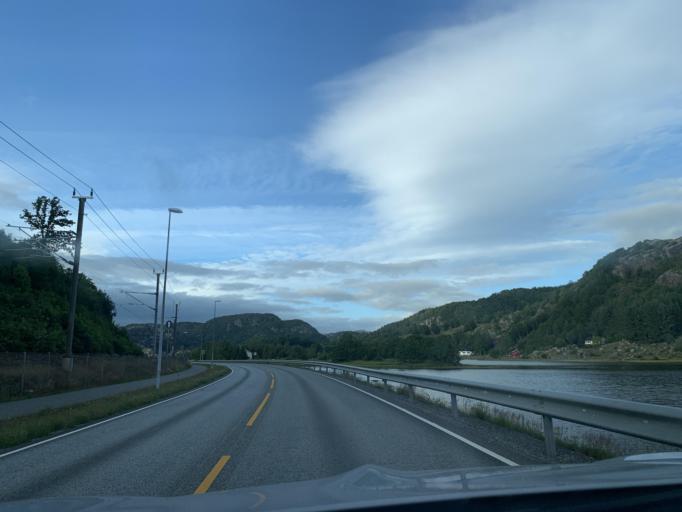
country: NO
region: Rogaland
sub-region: Eigersund
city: Egersund
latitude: 58.4638
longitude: 6.0218
